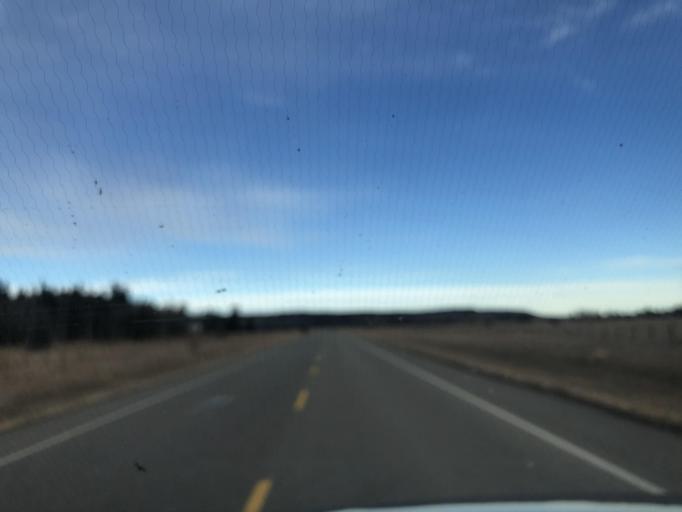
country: CA
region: Alberta
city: Cochrane
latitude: 51.0389
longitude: -114.7118
